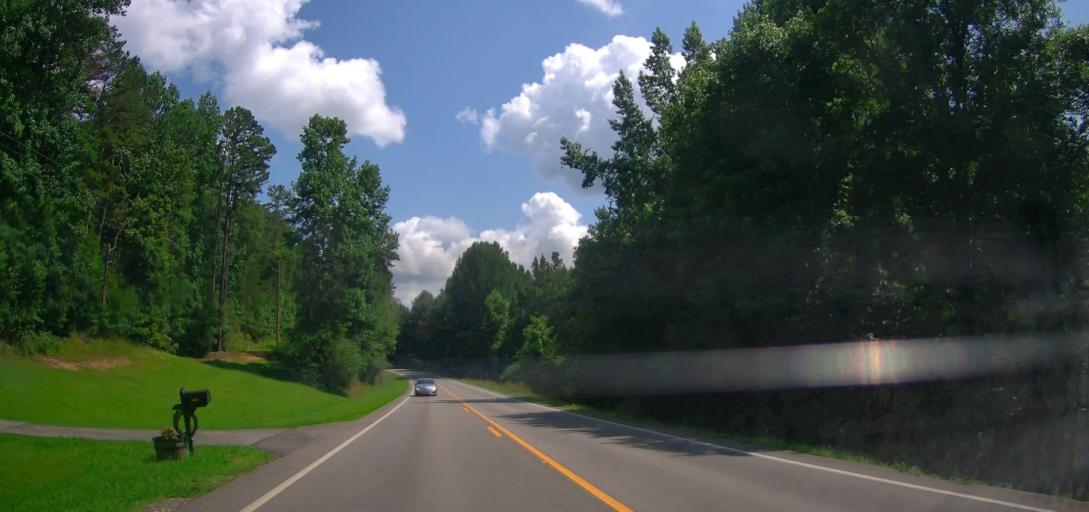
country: US
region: Alabama
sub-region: Cleburne County
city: Heflin
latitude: 33.6358
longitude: -85.4883
